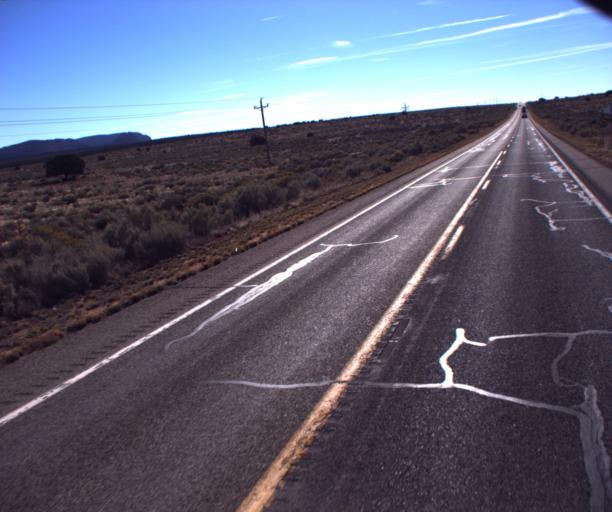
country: US
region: Arizona
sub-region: Mohave County
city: Colorado City
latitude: 36.9118
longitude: -112.9283
